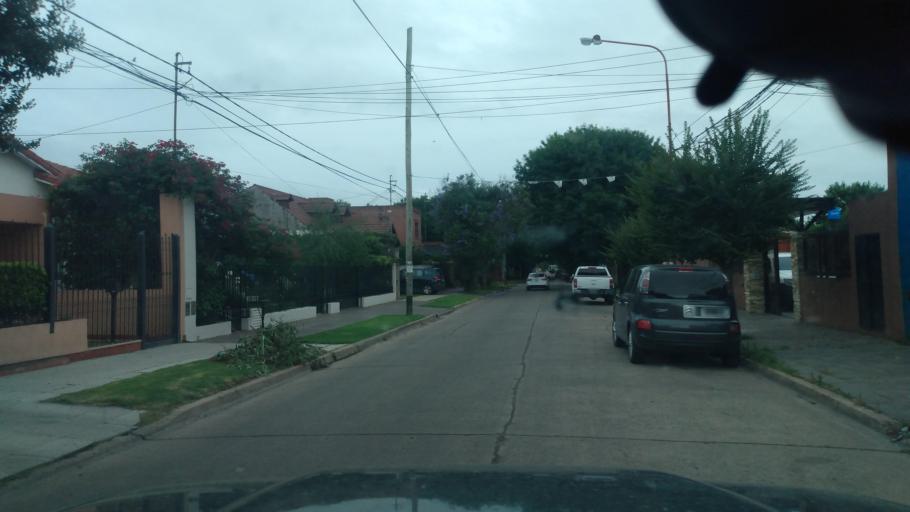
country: AR
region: Buenos Aires
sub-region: Partido de Lujan
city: Lujan
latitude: -34.5712
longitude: -59.1055
